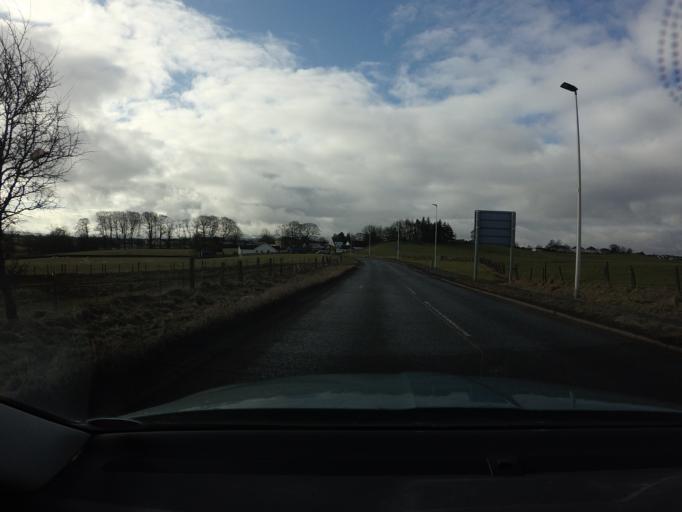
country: GB
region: Scotland
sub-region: South Lanarkshire
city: Carnwath
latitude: 55.6996
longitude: -3.6899
